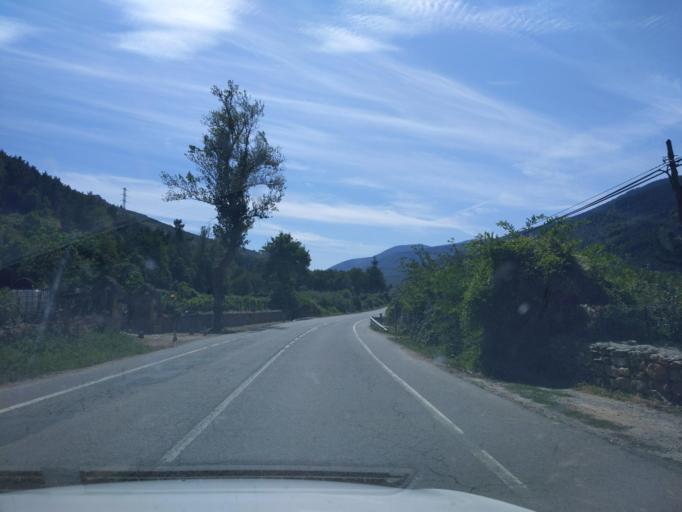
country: ES
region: La Rioja
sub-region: Provincia de La Rioja
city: Ezcaray
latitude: 42.3164
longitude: -3.0131
